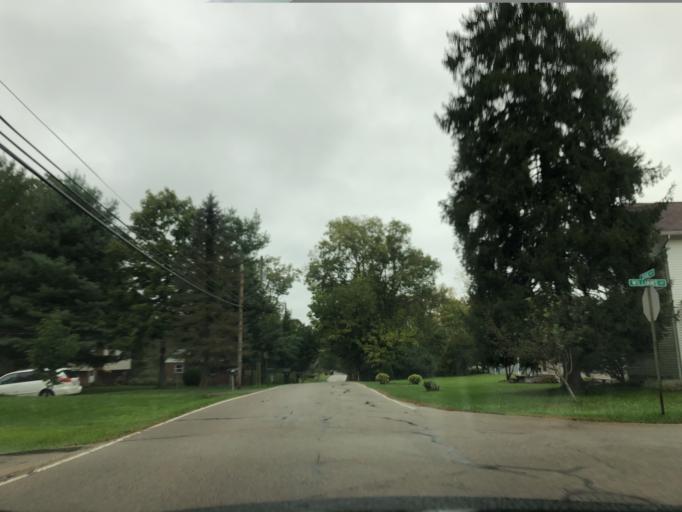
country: US
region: Ohio
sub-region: Hamilton County
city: Loveland
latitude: 39.2616
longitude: -84.2543
